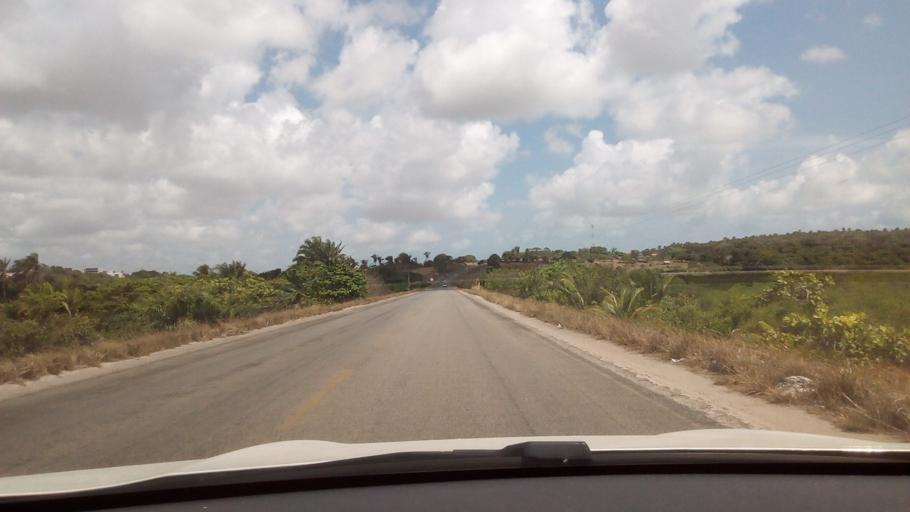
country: BR
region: Paraiba
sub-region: Conde
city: Conde
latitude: -7.2316
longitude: -34.8421
